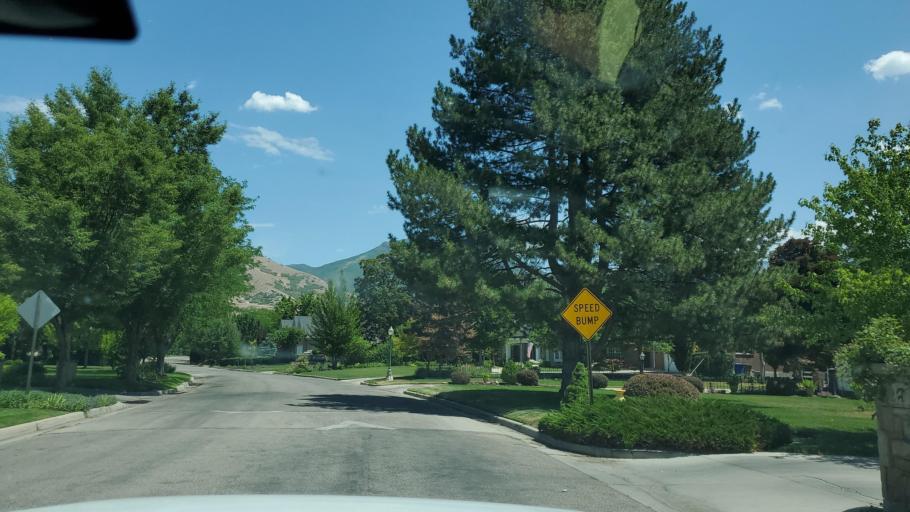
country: US
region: Utah
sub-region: Salt Lake County
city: Canyon Rim
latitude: 40.7174
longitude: -111.8292
